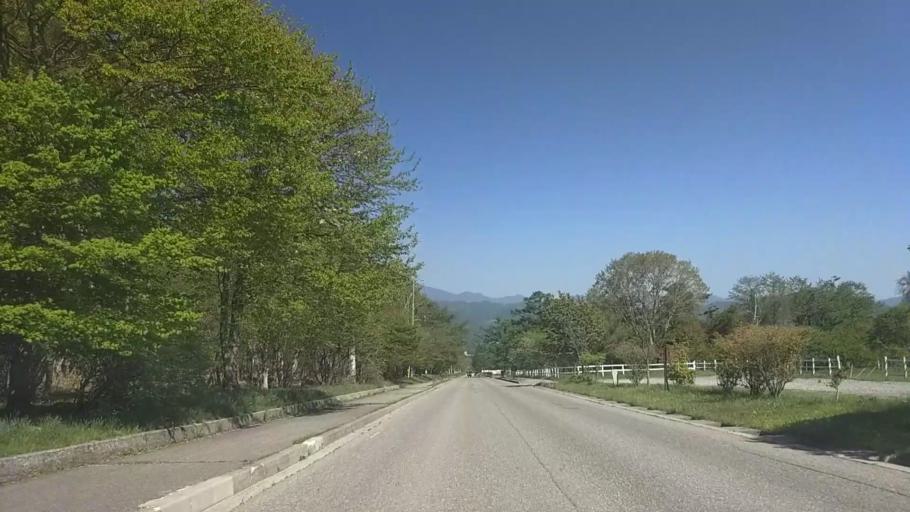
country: JP
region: Yamanashi
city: Nirasaki
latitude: 35.9243
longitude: 138.4226
